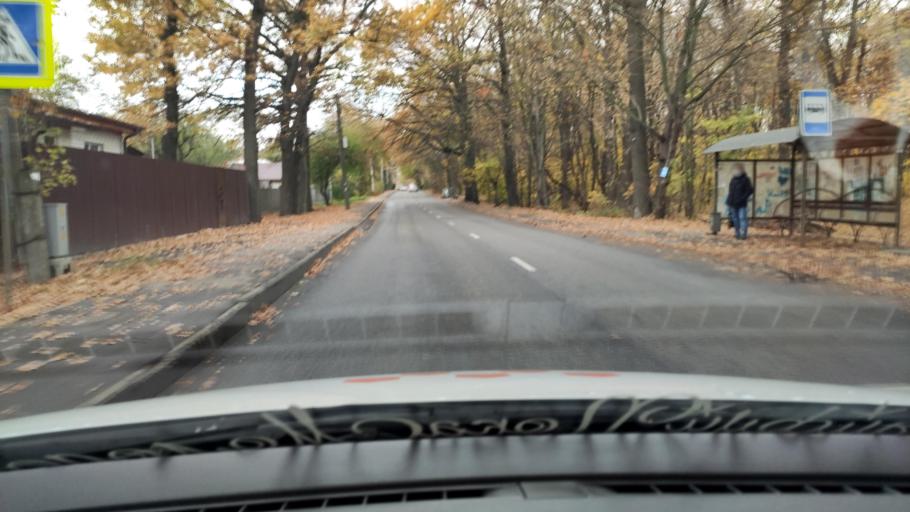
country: RU
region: Voronezj
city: Voronezh
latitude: 51.7235
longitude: 39.2206
